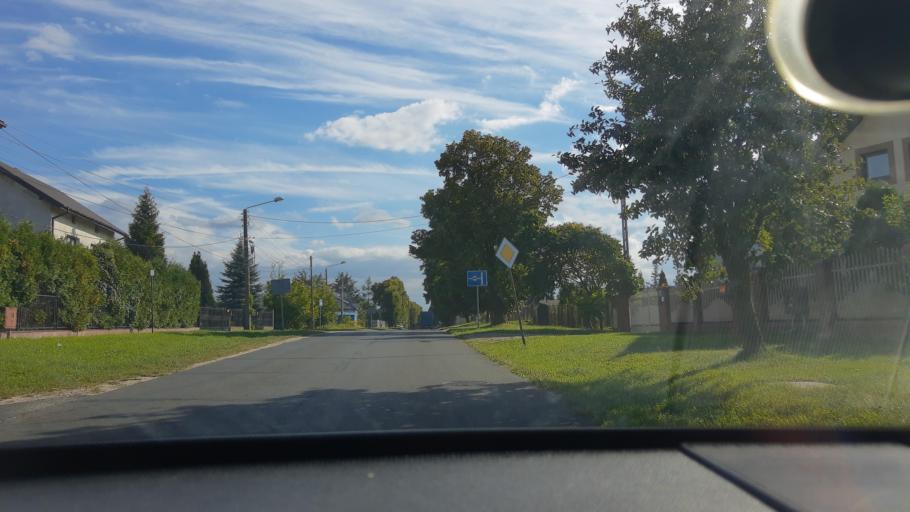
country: PL
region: Lodz Voivodeship
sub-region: Powiat sieradzki
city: Sieradz
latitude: 51.5777
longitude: 18.7369
